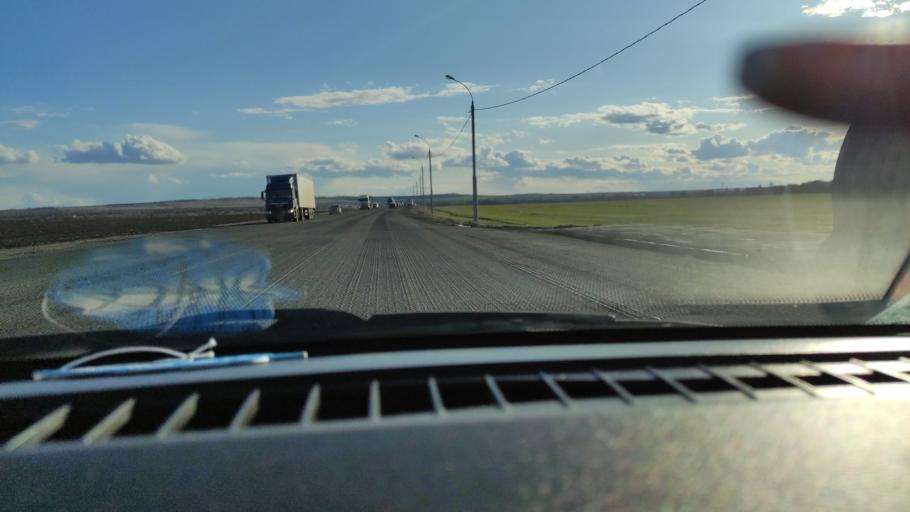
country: RU
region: Saratov
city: Yelshanka
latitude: 51.8113
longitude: 46.2020
